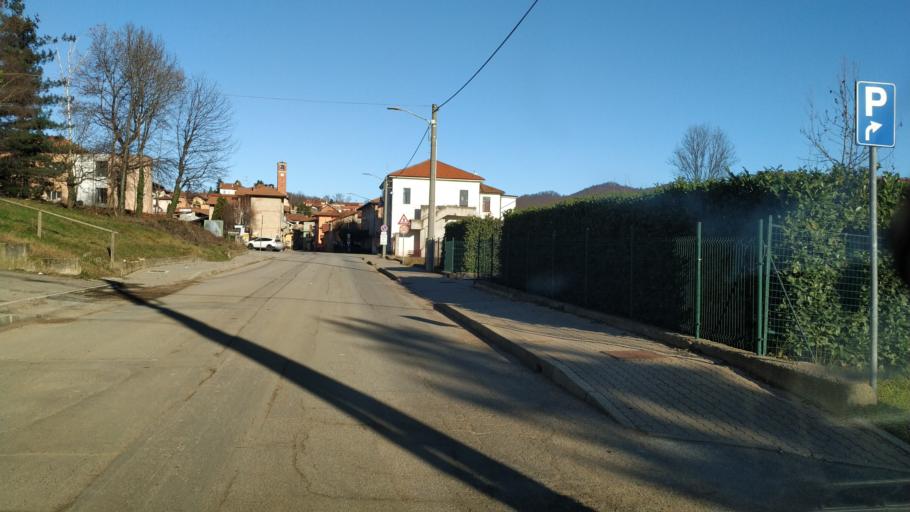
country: IT
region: Piedmont
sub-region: Provincia di Vercelli
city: Lozzolo
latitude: 45.6212
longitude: 8.3224
